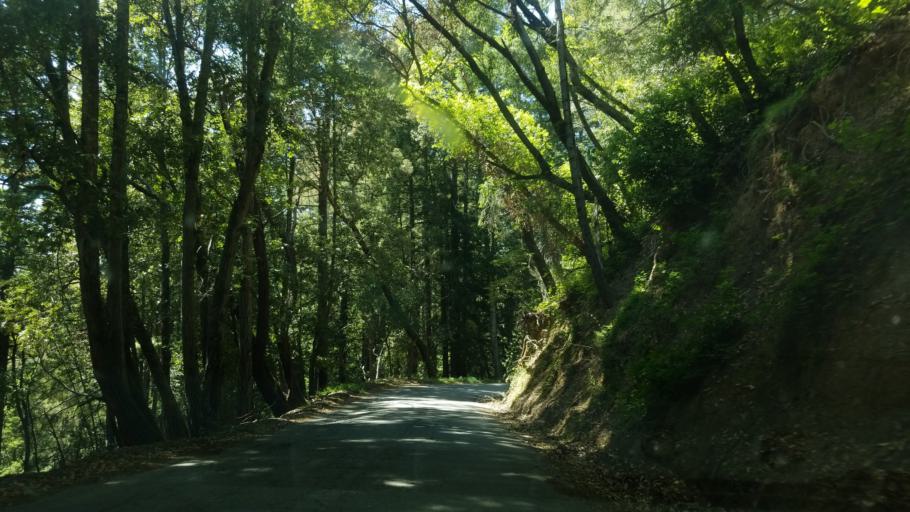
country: US
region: California
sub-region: Santa Cruz County
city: Day Valley
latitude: 37.0566
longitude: -121.8179
